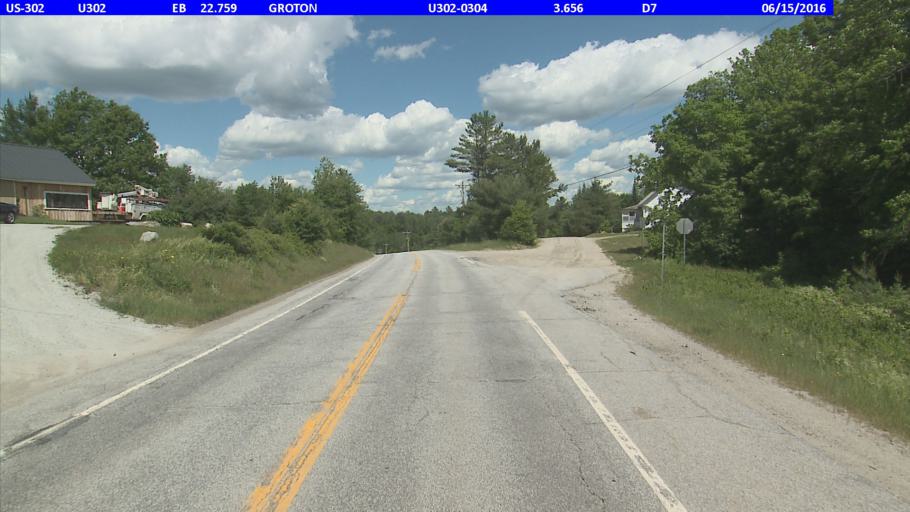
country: US
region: New Hampshire
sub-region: Grafton County
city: Woodsville
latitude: 44.2170
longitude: -72.2467
